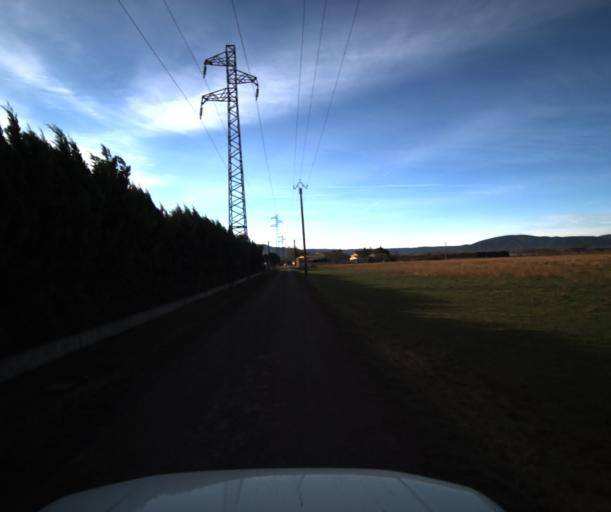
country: FR
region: Provence-Alpes-Cote d'Azur
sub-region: Departement du Vaucluse
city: Pertuis
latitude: 43.6861
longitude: 5.4740
